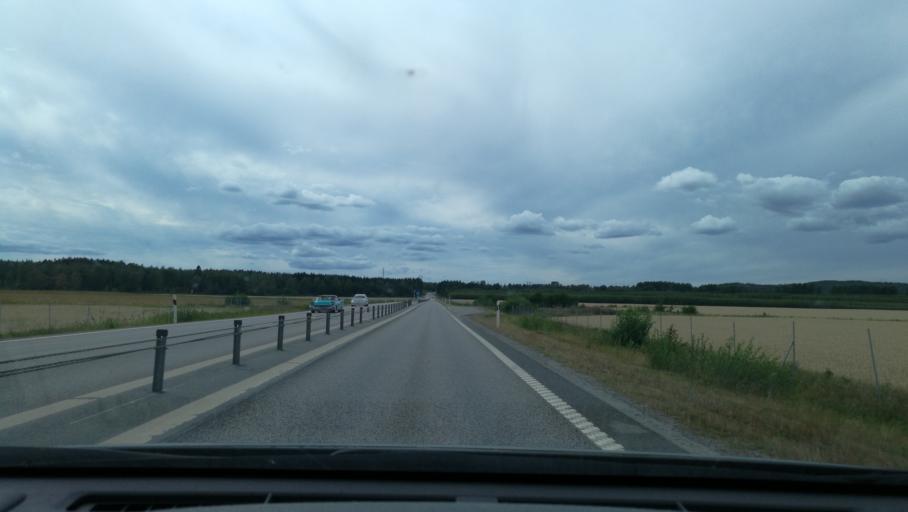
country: SE
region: OEstergoetland
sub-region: Norrkopings Kommun
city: Jursla
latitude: 58.6332
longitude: 16.1293
